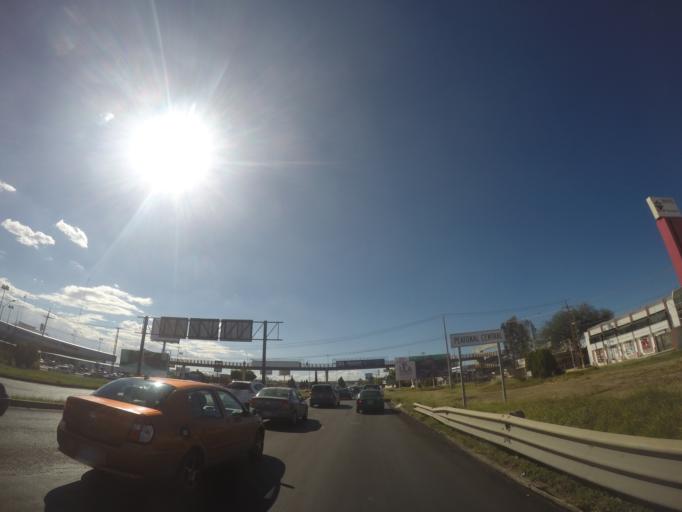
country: MX
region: San Luis Potosi
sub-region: San Luis Potosi
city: San Luis Potosi
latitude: 22.1472
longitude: -100.9509
